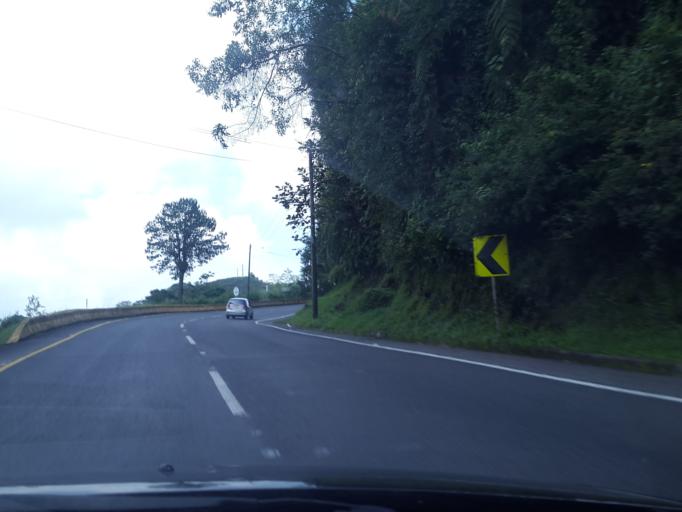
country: CO
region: Quindio
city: Filandia
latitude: 4.7091
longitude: -75.6037
